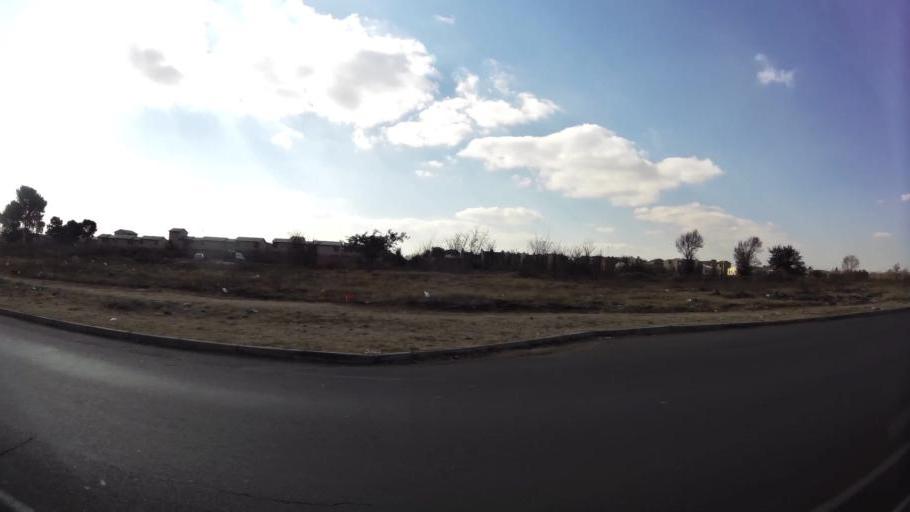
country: ZA
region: Gauteng
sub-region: City of Johannesburg Metropolitan Municipality
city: Soweto
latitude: -26.2797
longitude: 27.8952
